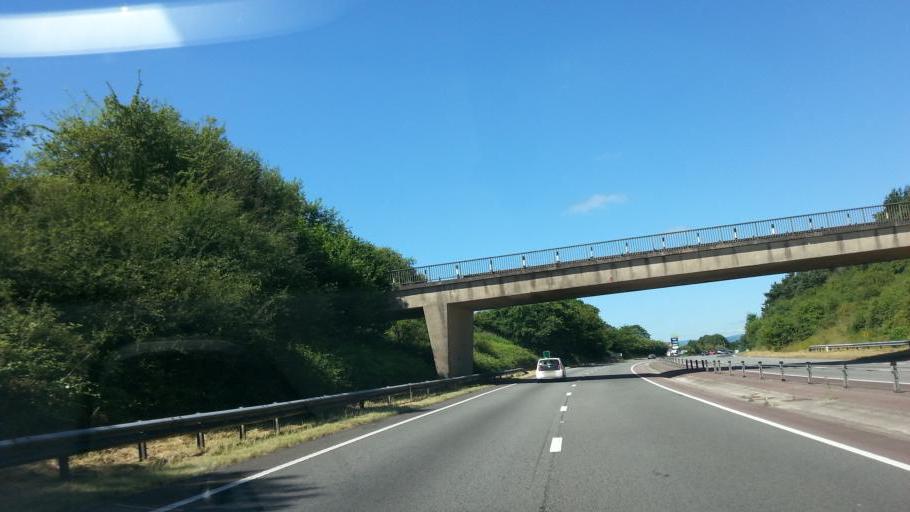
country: GB
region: Wales
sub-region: Monmouthshire
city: Mitchel Troy
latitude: 51.7728
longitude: -2.8066
